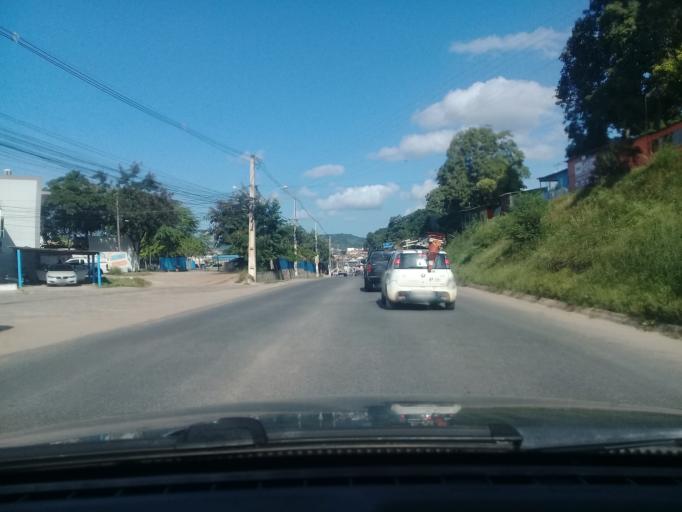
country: BR
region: Pernambuco
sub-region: Vitoria De Santo Antao
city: Vitoria de Santo Antao
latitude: -8.1126
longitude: -35.2882
